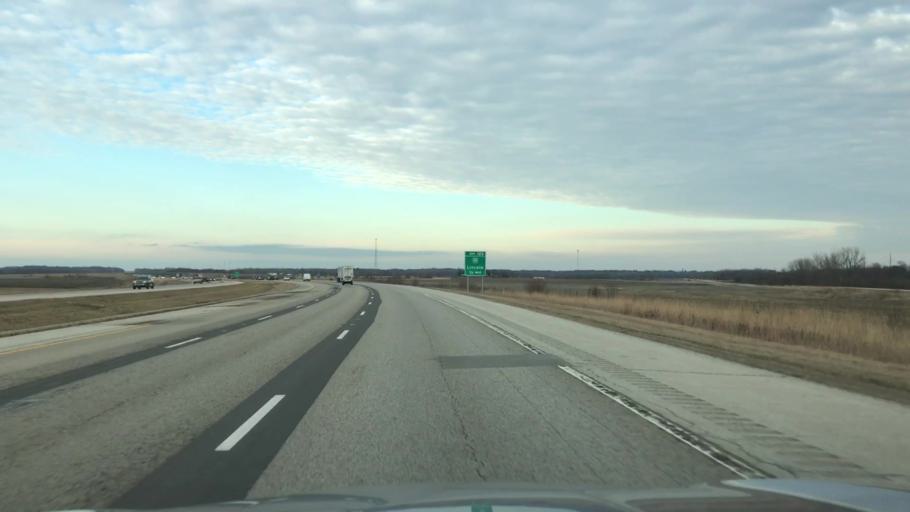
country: US
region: Illinois
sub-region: Logan County
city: Lincoln
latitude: 40.1009
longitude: -89.4167
